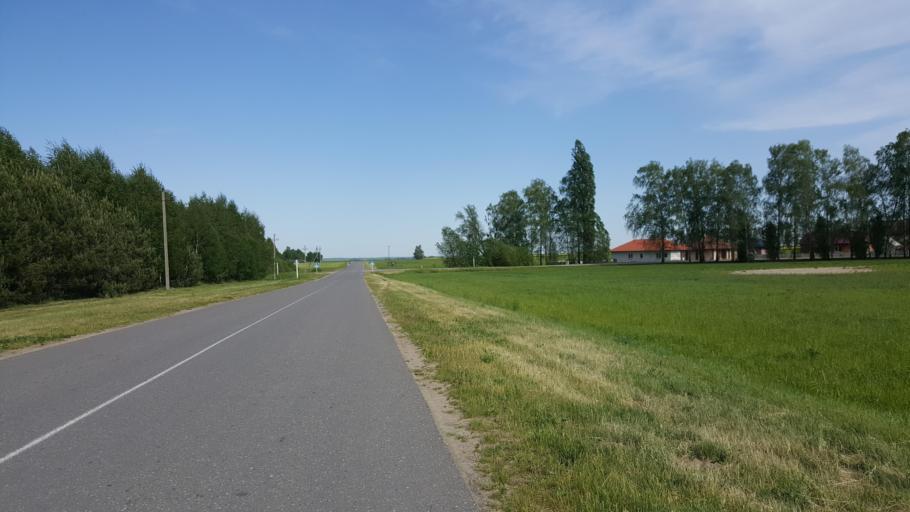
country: BY
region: Brest
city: Charnawchytsy
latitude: 52.2611
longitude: 23.5872
